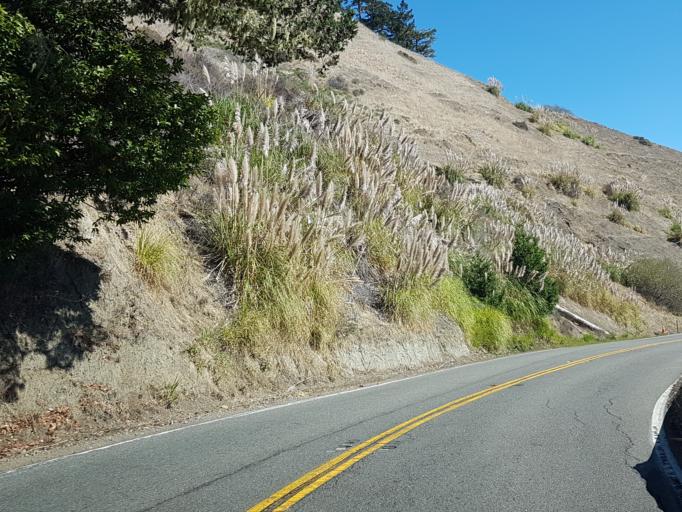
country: US
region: California
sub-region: Sonoma County
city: Monte Rio
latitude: 38.4976
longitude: -123.2031
